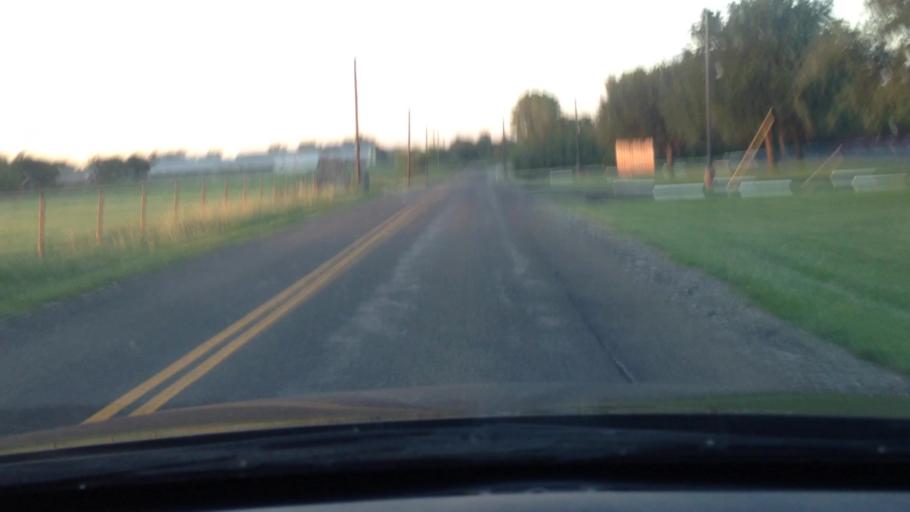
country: US
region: Texas
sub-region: Tarrant County
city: White Settlement
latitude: 32.7856
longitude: -97.4680
